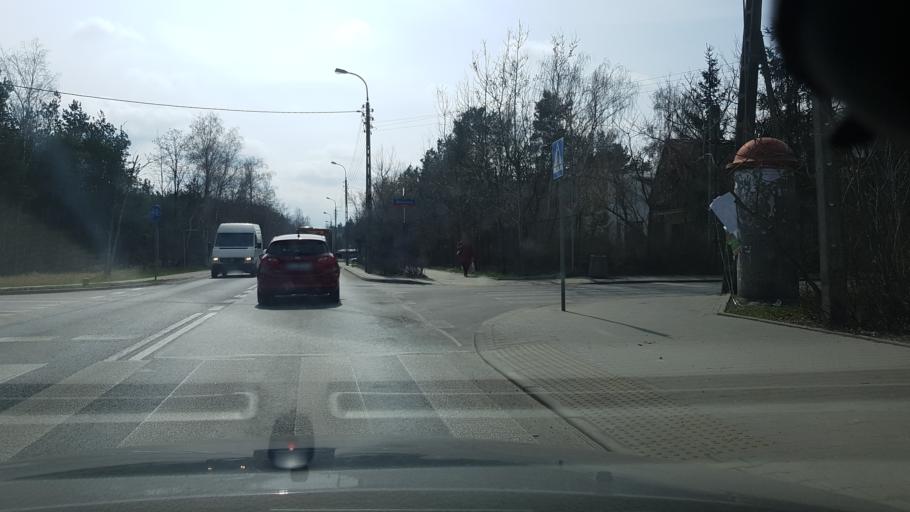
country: PL
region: Masovian Voivodeship
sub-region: Warszawa
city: Wesola
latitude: 52.2443
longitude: 21.2229
